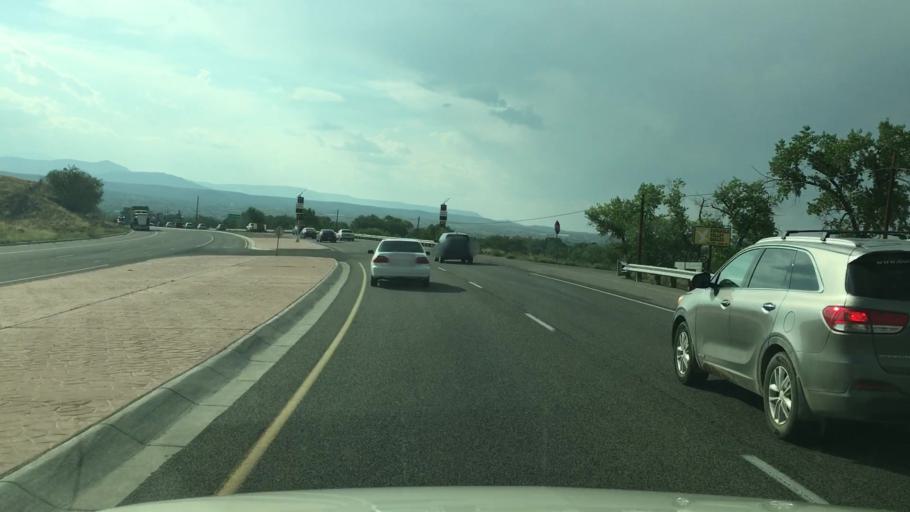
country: US
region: New Mexico
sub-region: Rio Arriba County
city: Espanola
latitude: 35.9854
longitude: -106.0525
